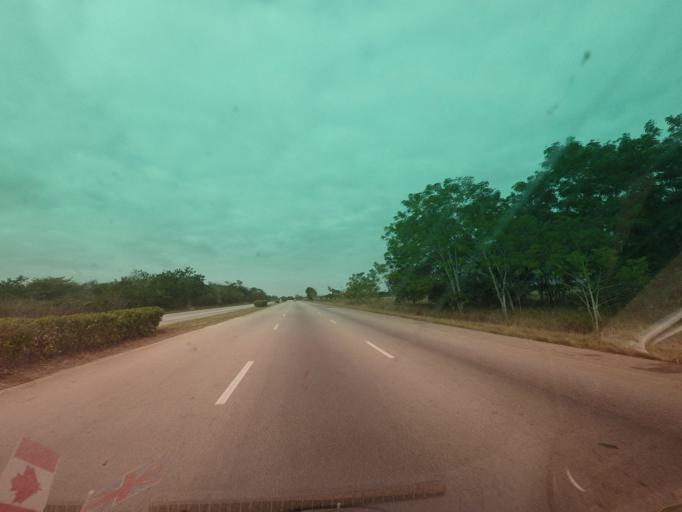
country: CU
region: Mayabeque
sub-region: Municipio de San Nicolas
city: San Nicolas de Bari
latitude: 22.7687
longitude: -81.7876
